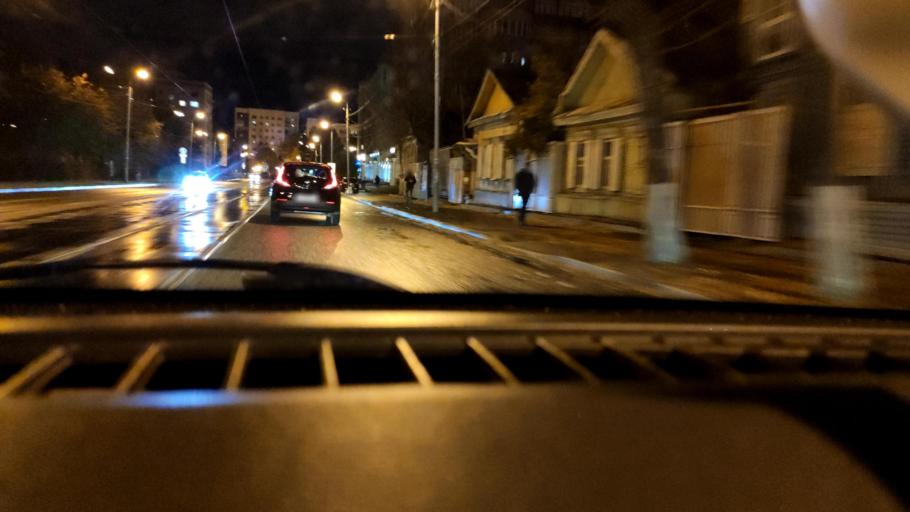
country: RU
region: Samara
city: Samara
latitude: 53.2048
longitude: 50.1197
